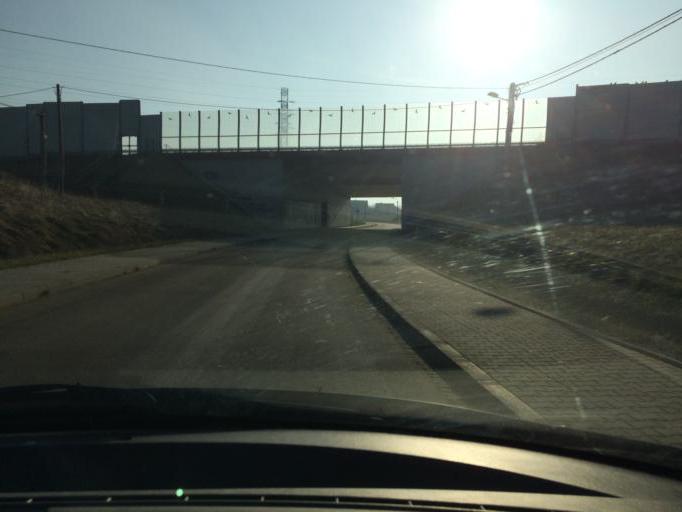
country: PL
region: Lesser Poland Voivodeship
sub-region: Powiat wielicki
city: Czarnochowice
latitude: 50.0068
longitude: 20.0440
